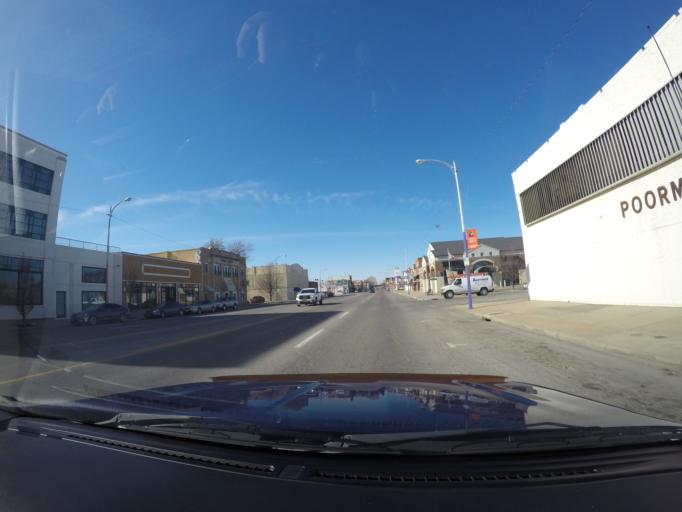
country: US
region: Kansas
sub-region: Sedgwick County
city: Wichita
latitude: 37.6862
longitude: -97.3204
